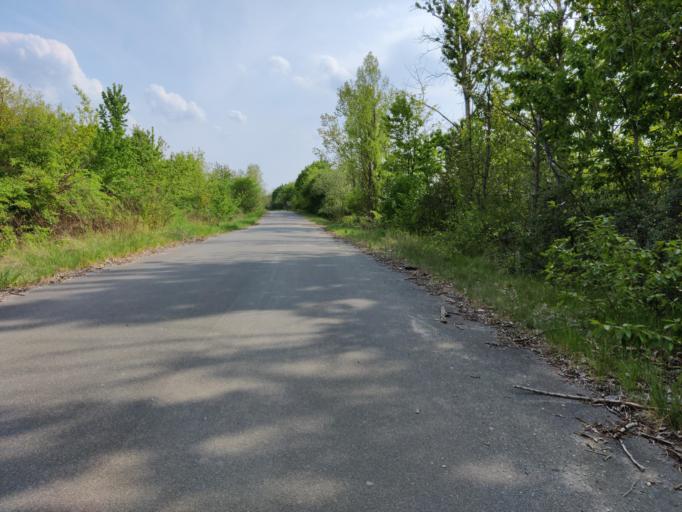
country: DE
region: Saxony
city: Markkleeberg
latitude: 51.2433
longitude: 12.3665
